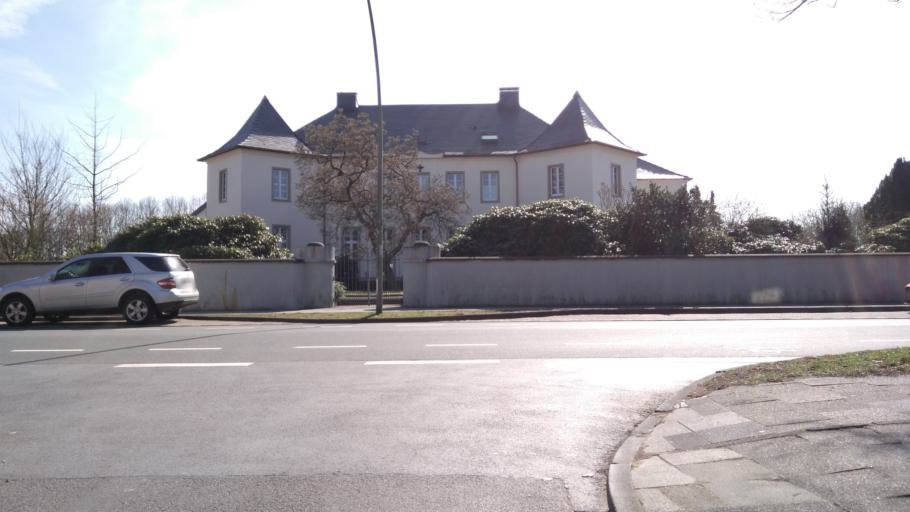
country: DE
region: North Rhine-Westphalia
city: Dorsten
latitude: 51.6057
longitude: 6.9276
